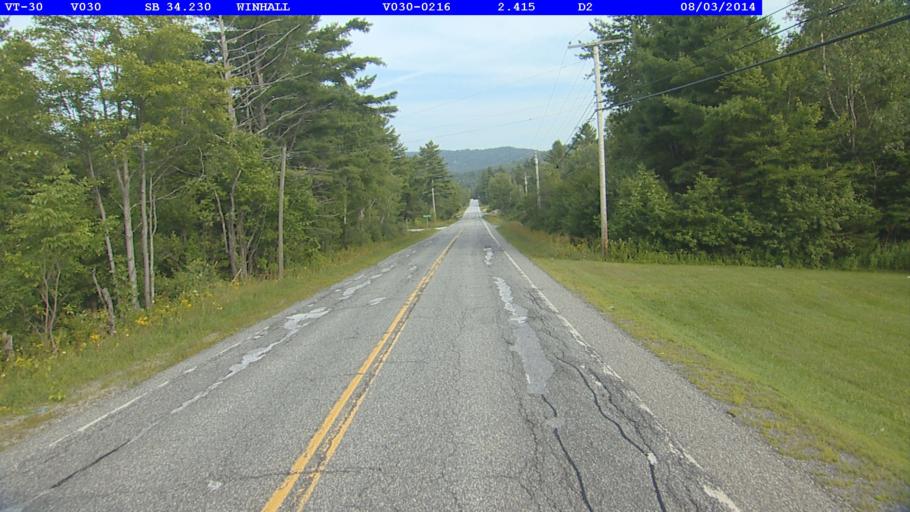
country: US
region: Vermont
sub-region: Bennington County
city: Manchester Center
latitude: 43.1530
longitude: -72.9098
